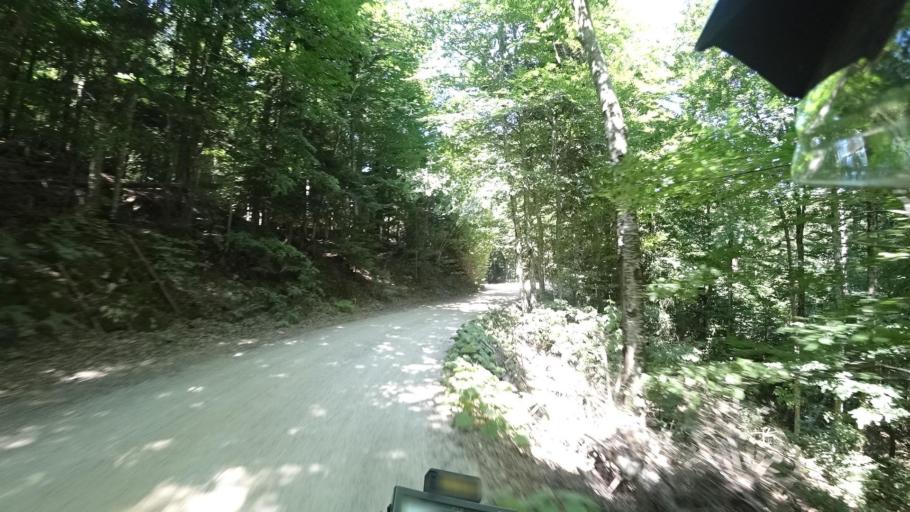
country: HR
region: Licko-Senjska
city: Popovaca
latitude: 44.5577
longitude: 15.2146
